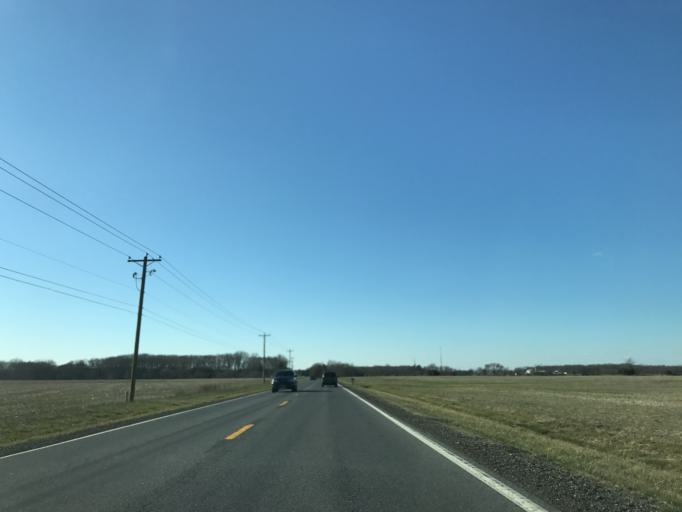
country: US
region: Maryland
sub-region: Queen Anne's County
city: Centreville
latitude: 39.0165
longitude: -76.0028
